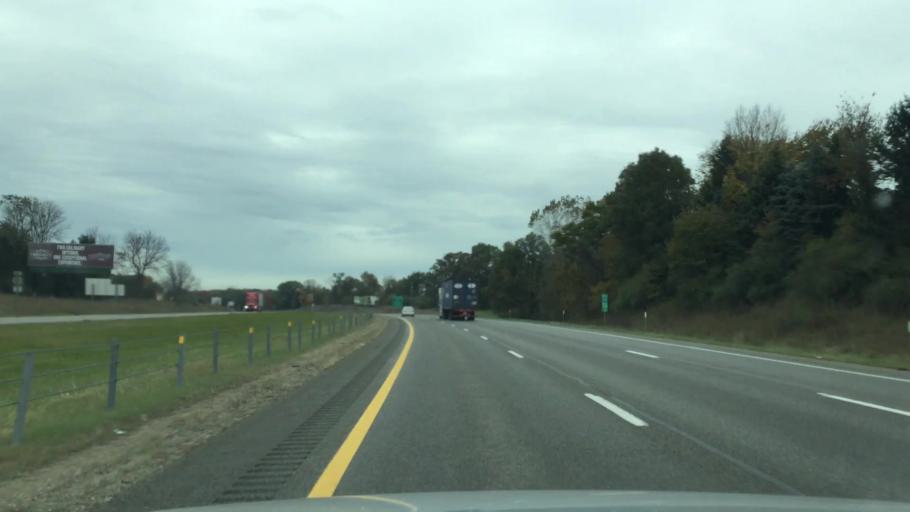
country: US
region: Michigan
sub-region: Calhoun County
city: Marshall
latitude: 42.2962
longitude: -84.9692
